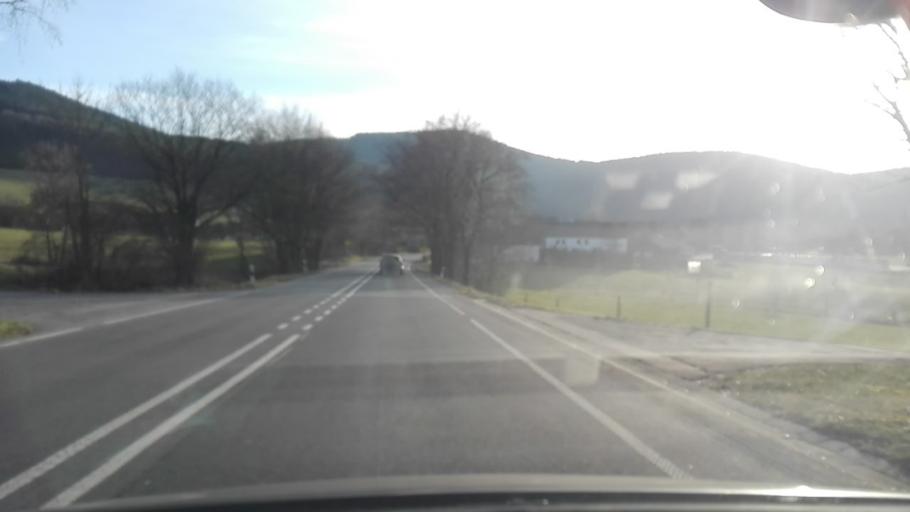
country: DE
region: North Rhine-Westphalia
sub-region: Regierungsbezirk Arnsberg
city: Schmallenberg
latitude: 51.1613
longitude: 8.1989
